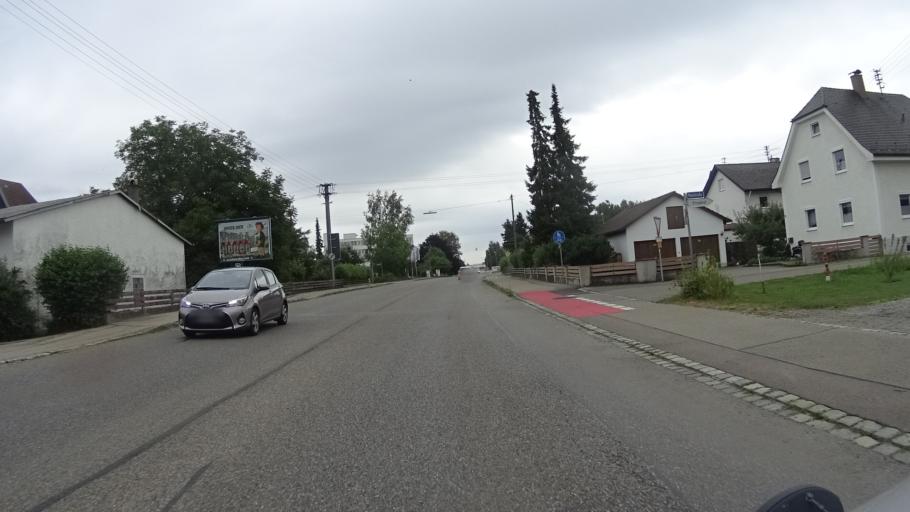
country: DE
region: Bavaria
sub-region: Swabia
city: Heimertingen
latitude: 48.0133
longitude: 10.1635
